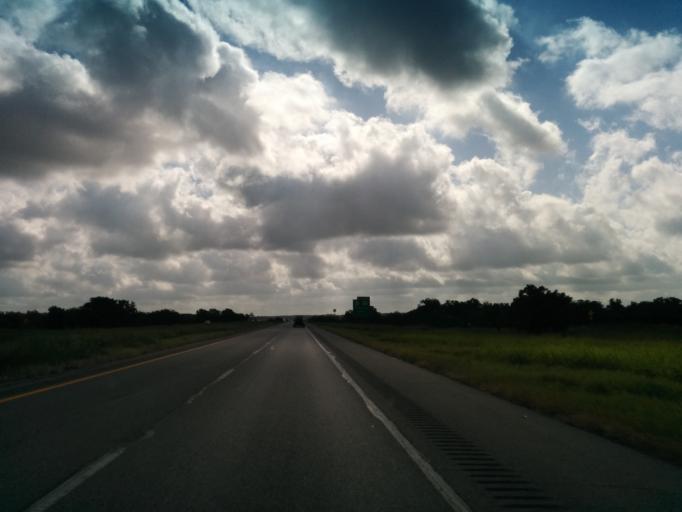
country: US
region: Texas
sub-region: Caldwell County
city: Luling
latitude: 29.6500
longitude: -97.6068
